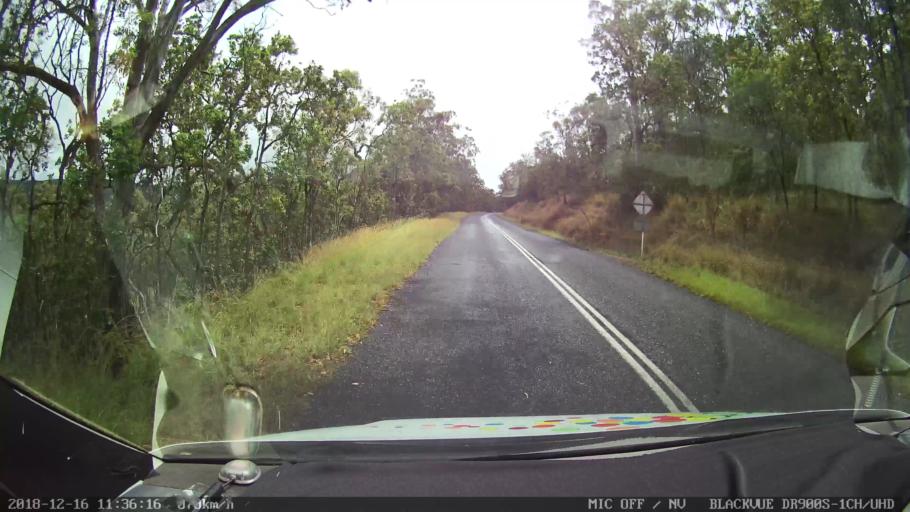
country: AU
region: New South Wales
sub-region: Tenterfield Municipality
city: Carrolls Creek
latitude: -28.9825
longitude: 152.1692
